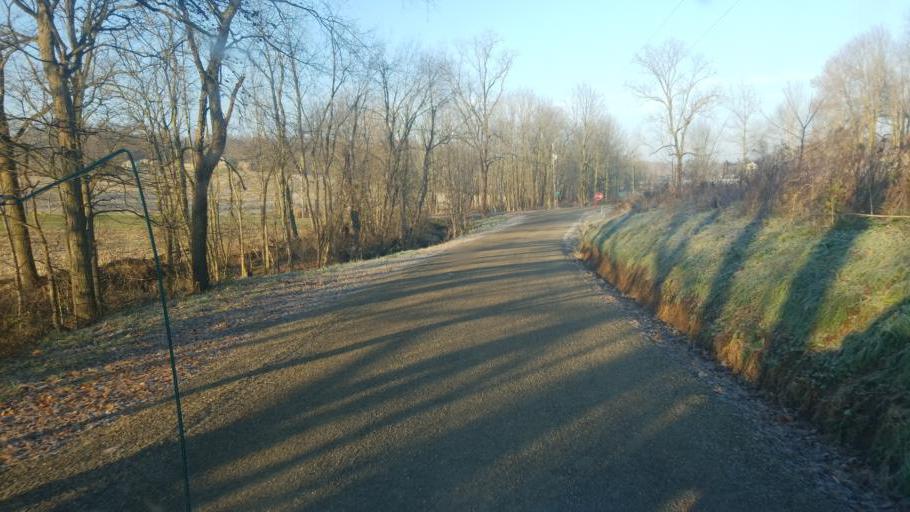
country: US
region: Ohio
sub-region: Knox County
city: Danville
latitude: 40.4463
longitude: -82.3075
